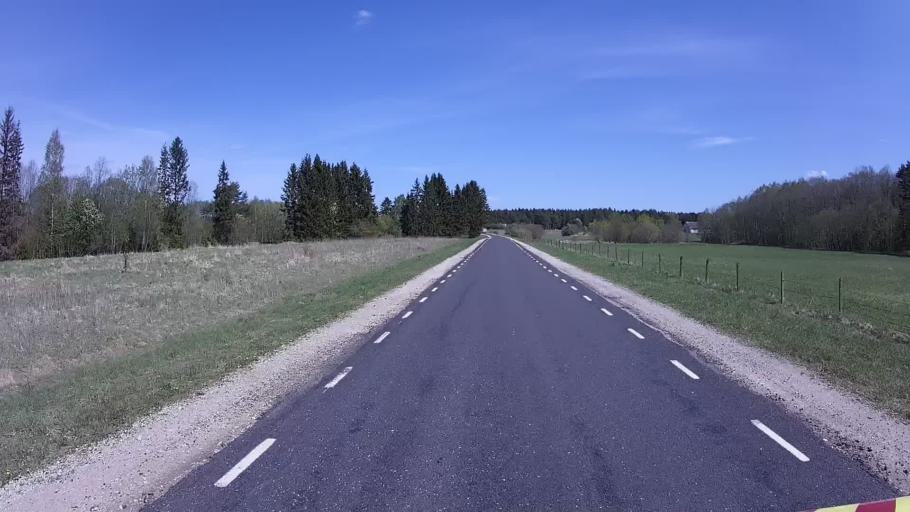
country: EE
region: Laeaene
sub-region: Ridala Parish
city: Uuemoisa
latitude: 59.0282
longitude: 23.8137
